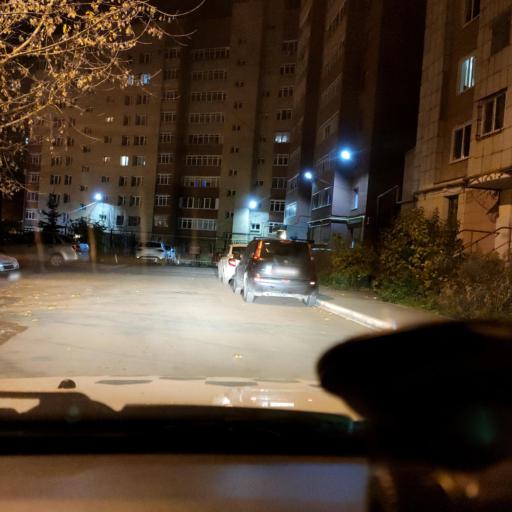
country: RU
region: Perm
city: Perm
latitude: 58.0980
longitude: 56.2984
